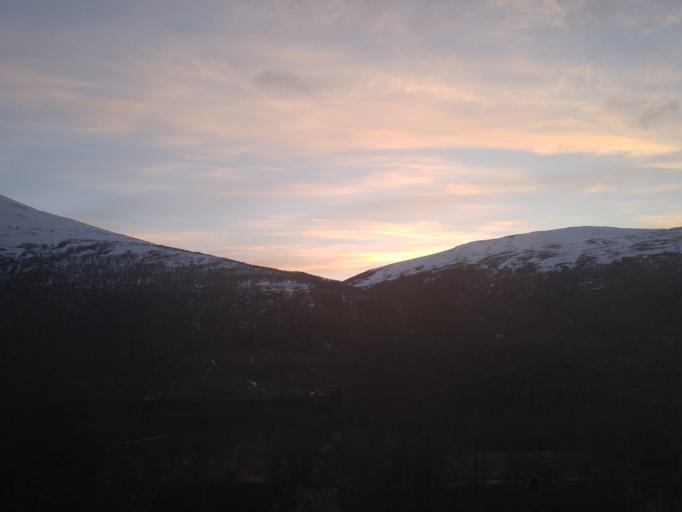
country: NO
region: Sor-Trondelag
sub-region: Oppdal
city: Oppdal
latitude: 62.5263
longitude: 9.6125
